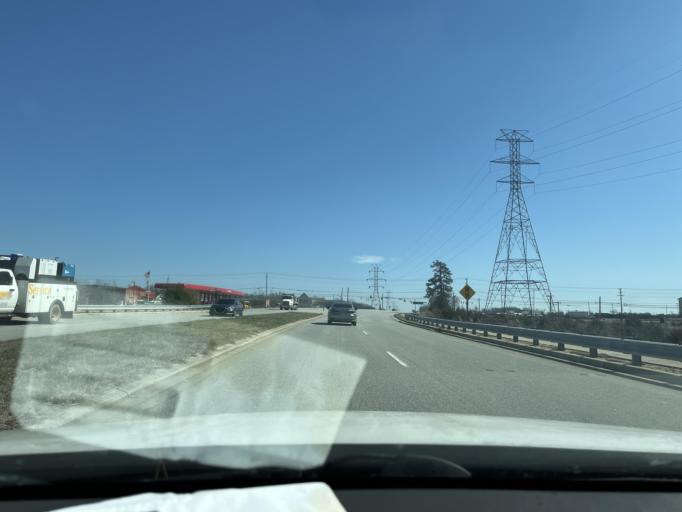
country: US
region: North Carolina
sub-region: Guilford County
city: Jamestown
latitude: 36.0021
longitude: -79.9102
